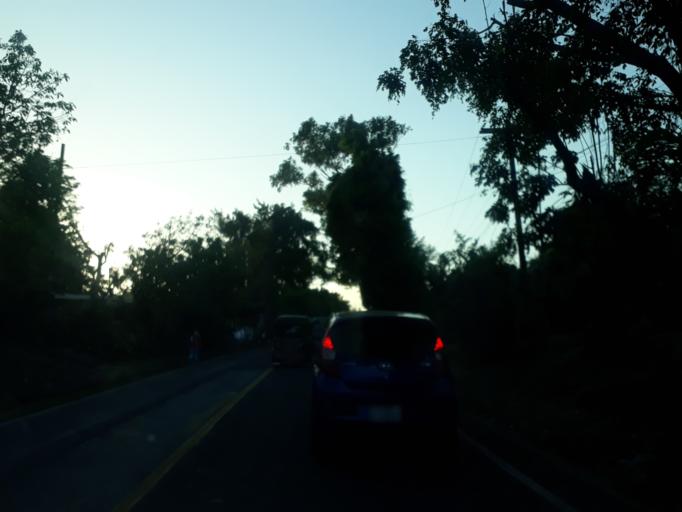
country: NI
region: Masaya
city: Niquinohomo
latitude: 11.8998
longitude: -86.1153
